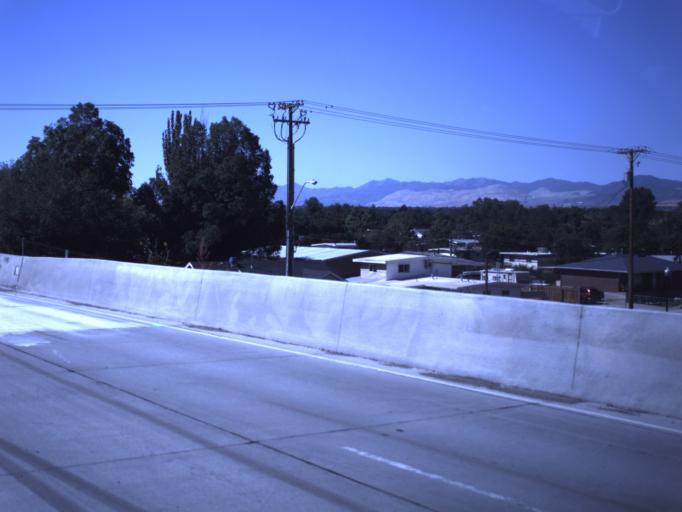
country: US
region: Utah
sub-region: Salt Lake County
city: Taylorsville
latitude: 40.6898
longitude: -111.9521
